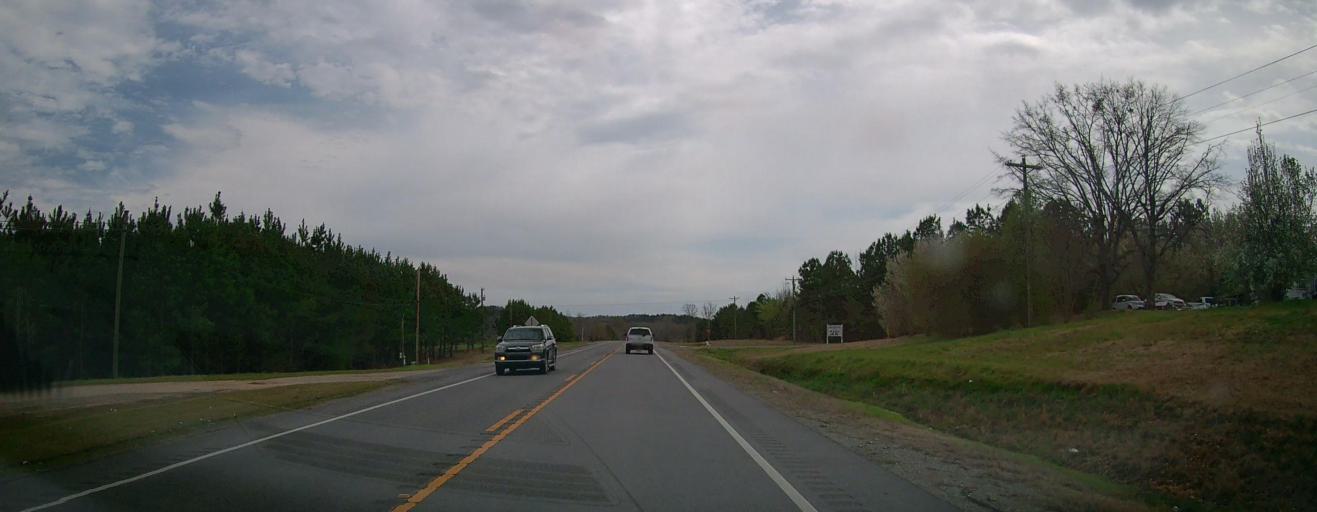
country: US
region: Alabama
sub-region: Marion County
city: Guin
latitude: 34.0077
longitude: -87.9340
